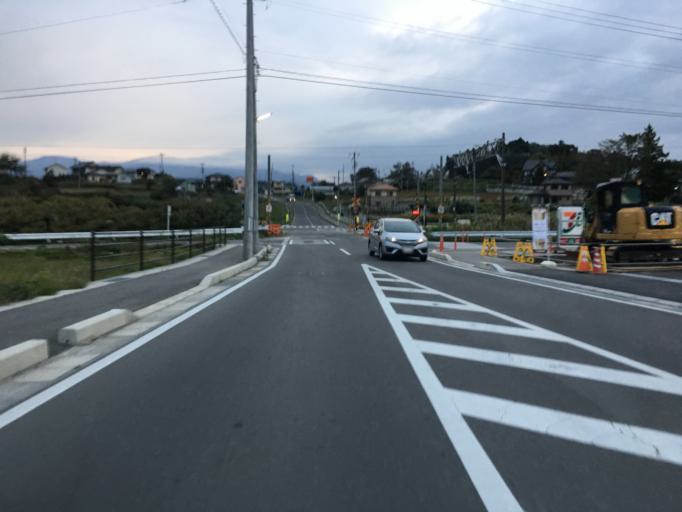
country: JP
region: Fukushima
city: Nihommatsu
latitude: 37.6149
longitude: 140.4685
